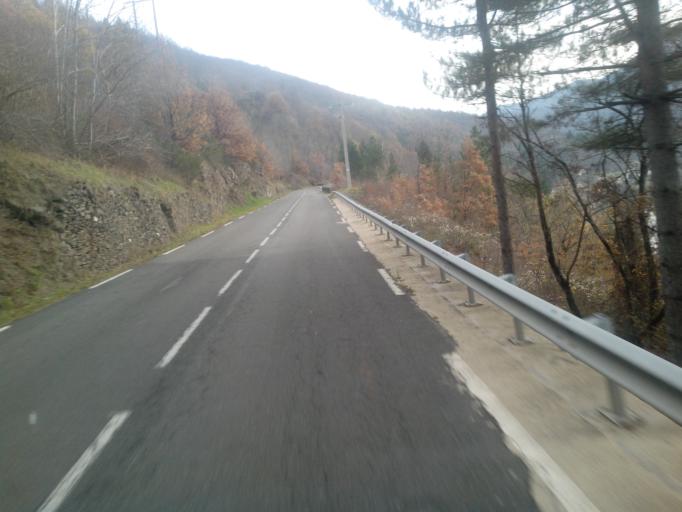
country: FR
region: Languedoc-Roussillon
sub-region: Departement de la Lozere
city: Florac
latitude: 44.3755
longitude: 3.5545
